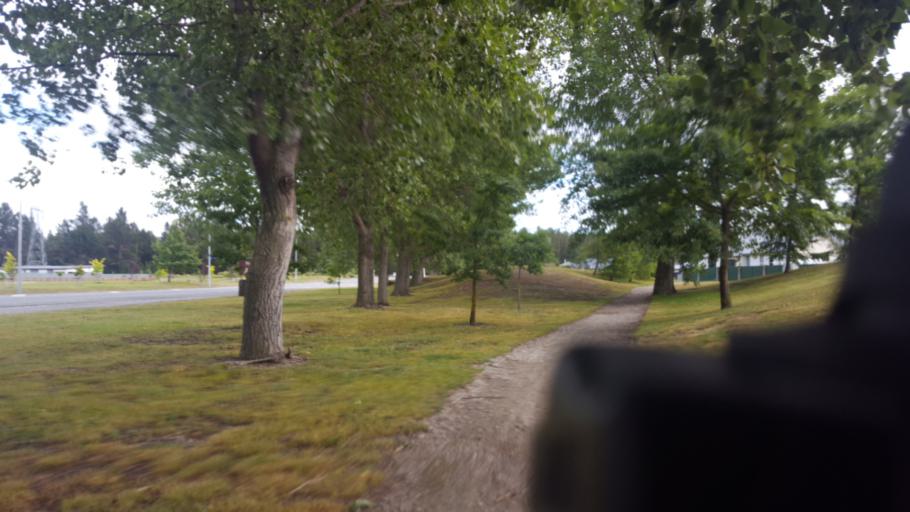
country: NZ
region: Otago
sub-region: Queenstown-Lakes District
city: Wanaka
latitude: -45.2425
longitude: 169.3778
